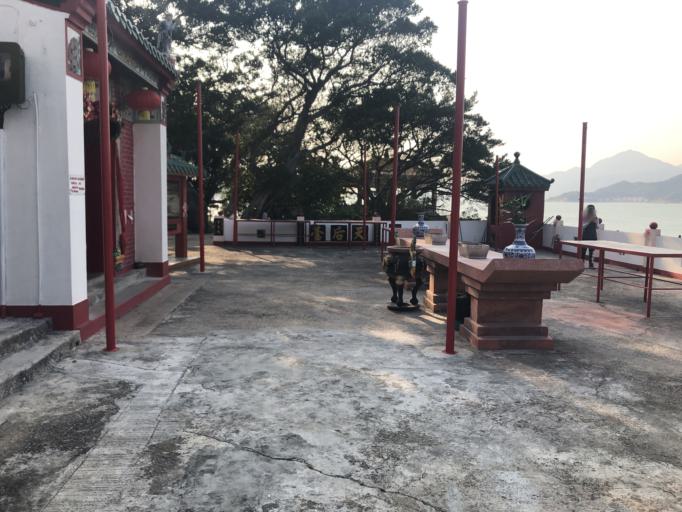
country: HK
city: Yung Shue Wan
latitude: 22.2015
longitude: 114.0190
